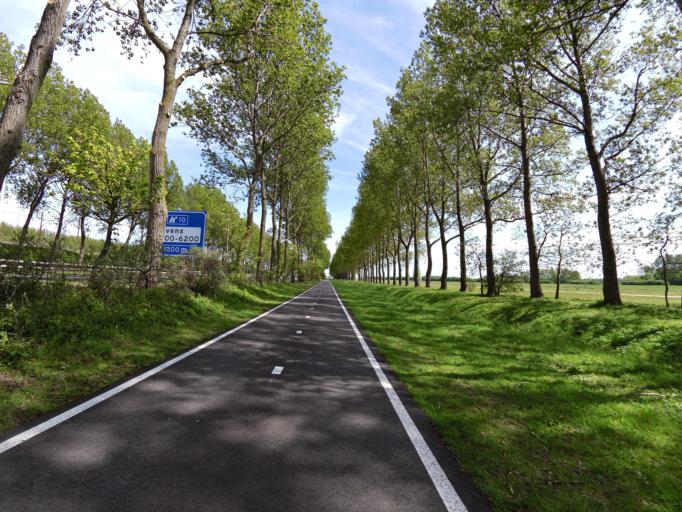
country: NL
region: South Holland
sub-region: Gemeente Rotterdam
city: Hoek van Holland
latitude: 51.9370
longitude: 4.1217
